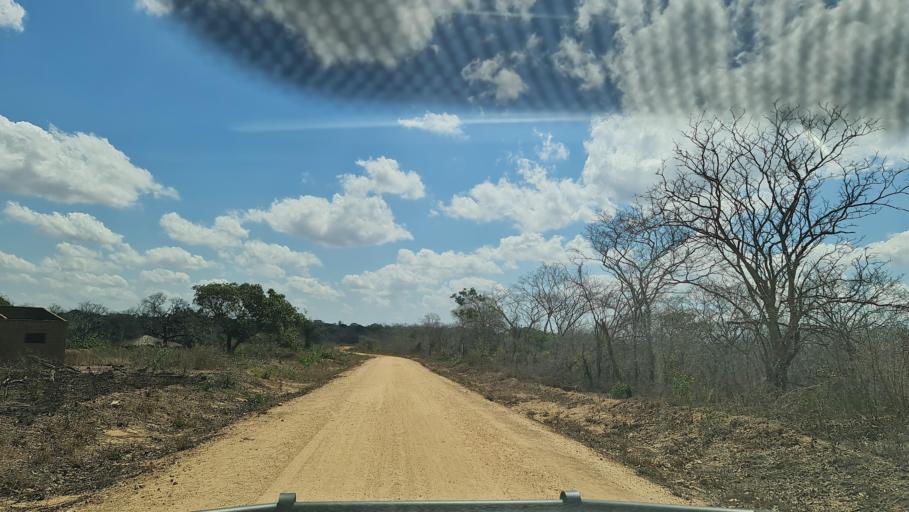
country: MZ
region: Nampula
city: Nacala
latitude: -14.1788
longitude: 40.2245
